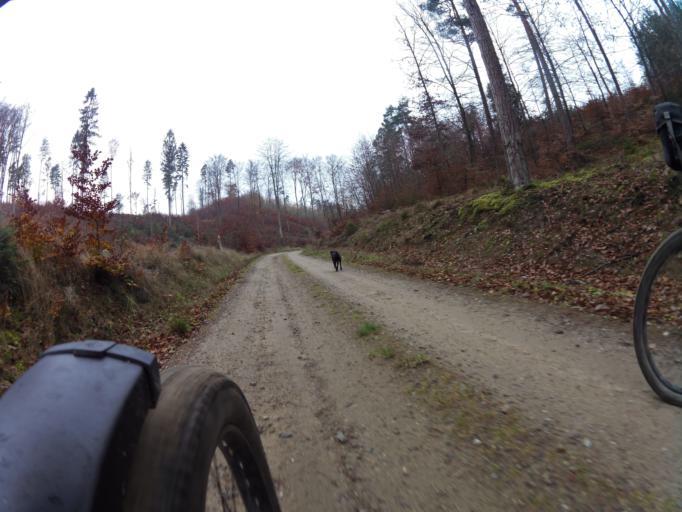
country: PL
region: Pomeranian Voivodeship
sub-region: Powiat pucki
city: Krokowa
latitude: 54.7119
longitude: 18.1432
